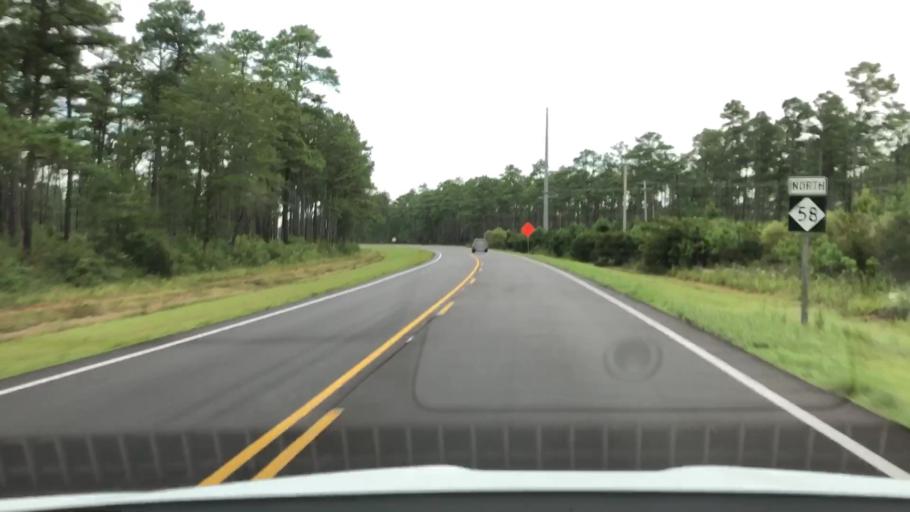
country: US
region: North Carolina
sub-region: Onslow County
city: Swansboro
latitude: 34.8082
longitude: -77.1346
